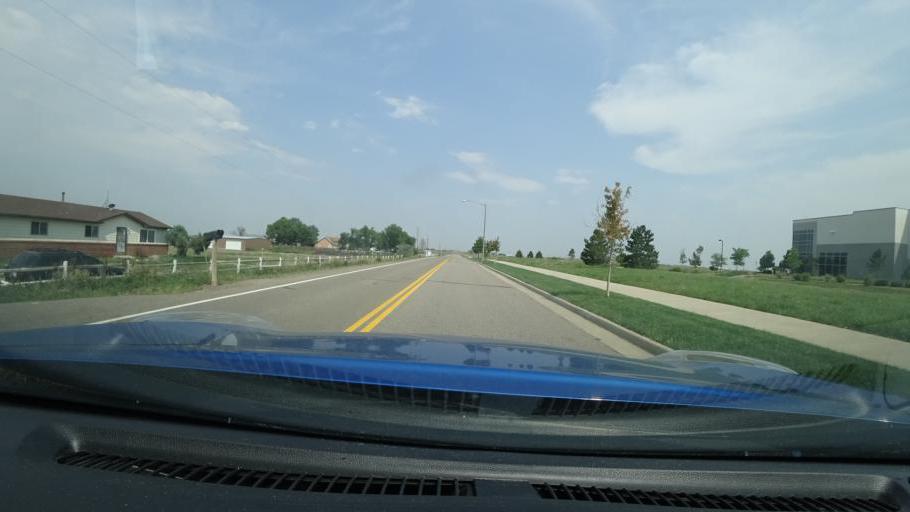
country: US
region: Colorado
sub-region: Adams County
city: Aurora
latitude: 39.7547
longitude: -104.7304
